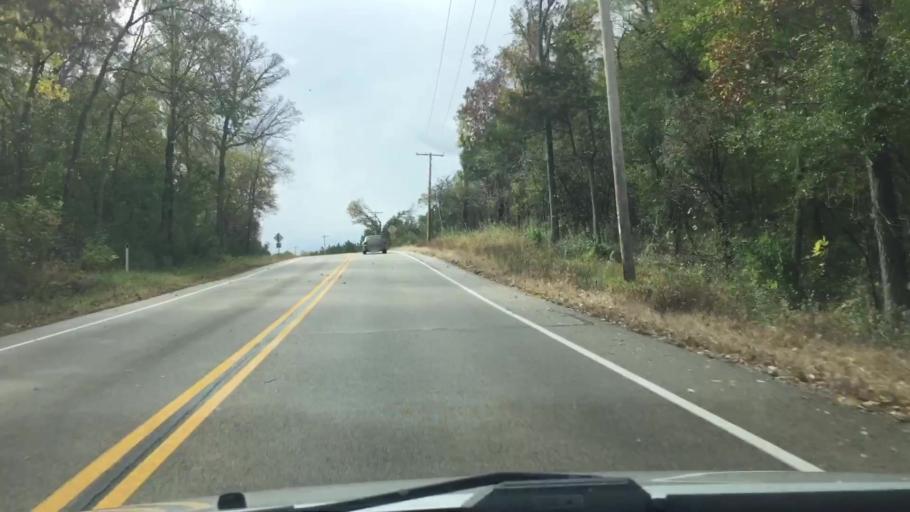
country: US
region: Wisconsin
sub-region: Waukesha County
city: Dousman
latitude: 42.9819
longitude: -88.4650
